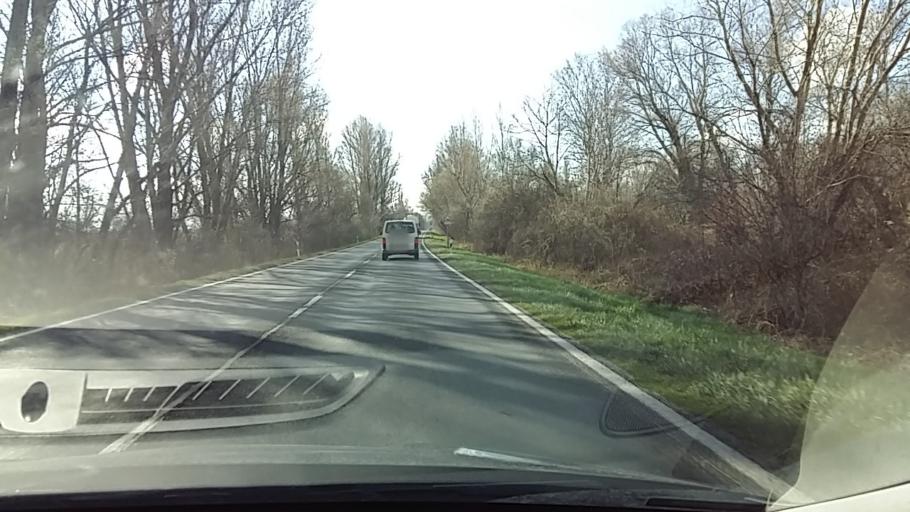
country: HU
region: Veszprem
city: Tapolca
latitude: 46.8283
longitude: 17.3784
